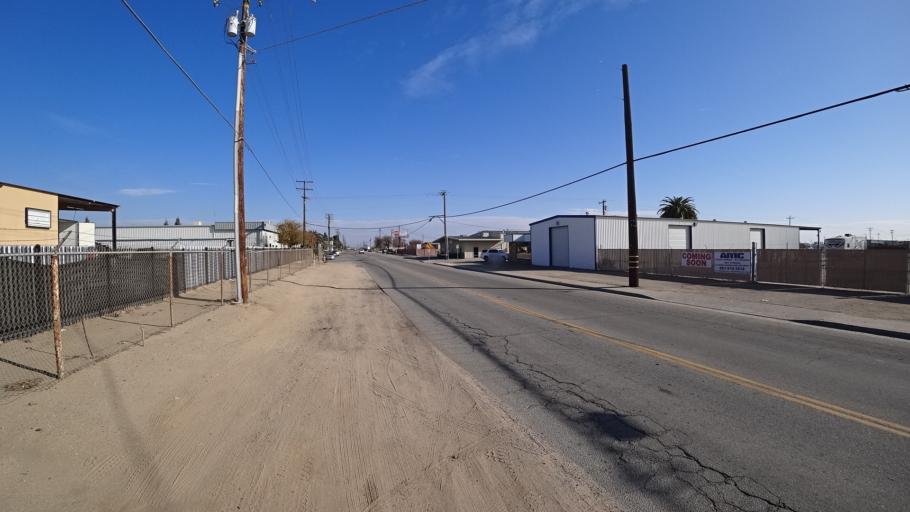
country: US
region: California
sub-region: Kern County
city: Greenacres
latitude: 35.3906
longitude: -119.0818
